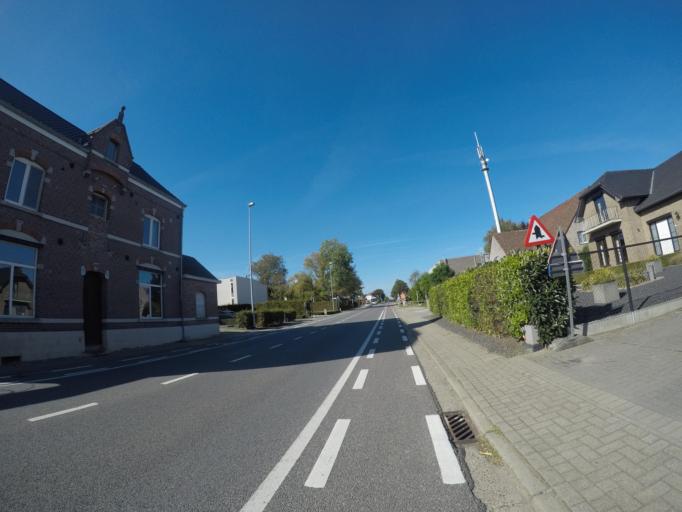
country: BE
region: Flanders
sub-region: Provincie Limburg
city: Alken
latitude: 50.8880
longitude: 5.2916
